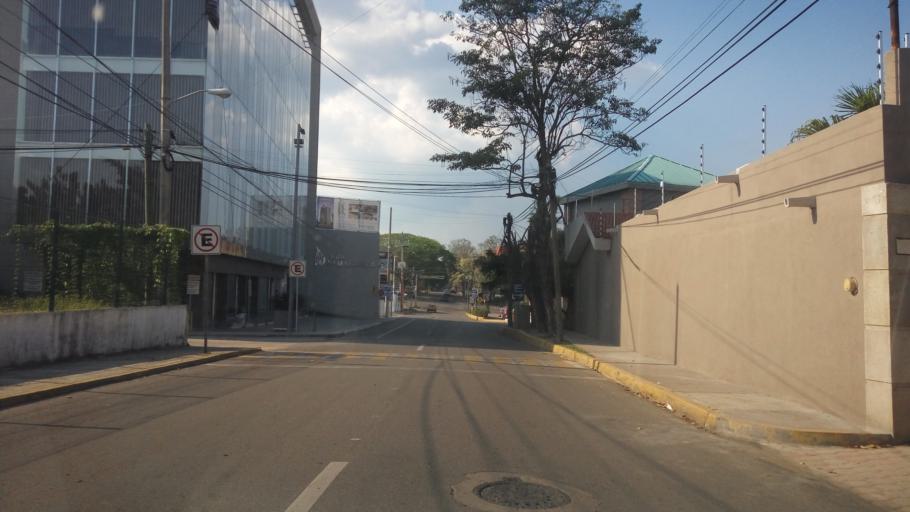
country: MX
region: Tabasco
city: Villahermosa
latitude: 18.0001
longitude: -92.9409
